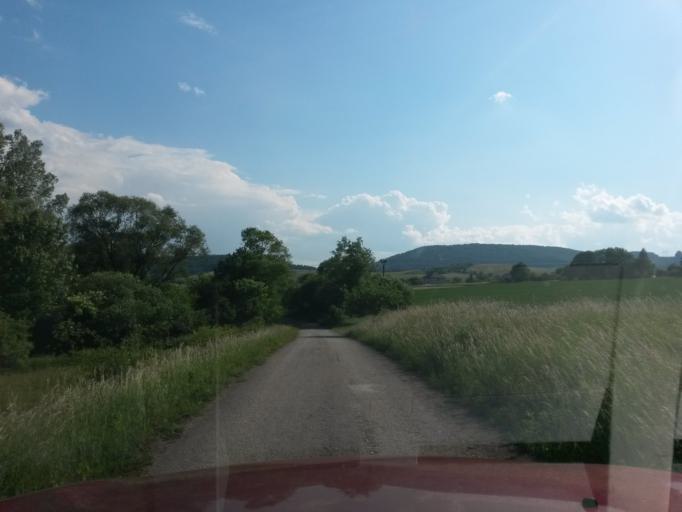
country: SK
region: Kosicky
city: Roznava
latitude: 48.5851
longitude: 20.6422
